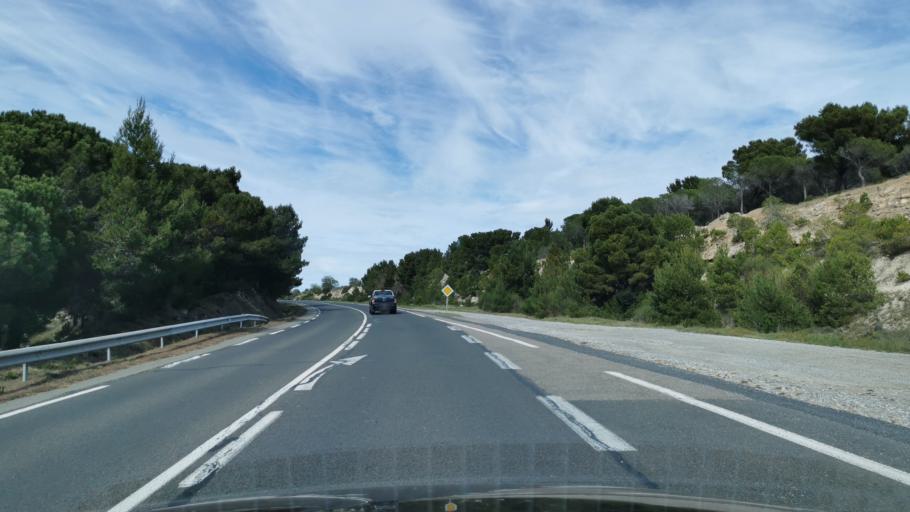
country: FR
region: Languedoc-Roussillon
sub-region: Departement de l'Aude
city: Leucate
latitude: 42.9156
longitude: 3.0214
